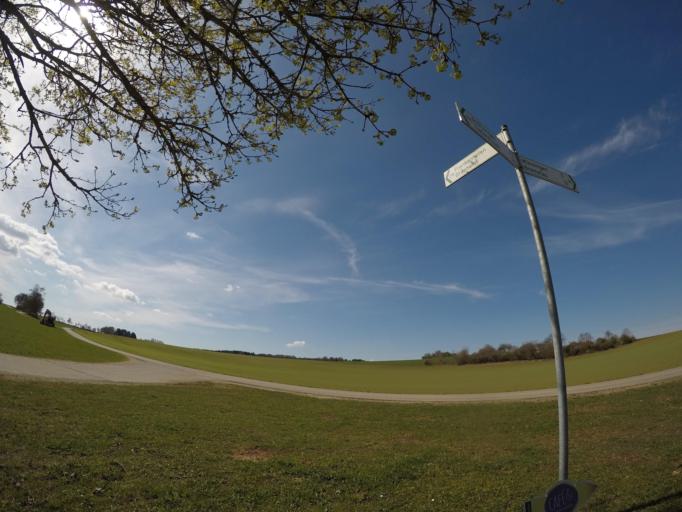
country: DE
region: Baden-Wuerttemberg
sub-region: Tuebingen Region
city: Mehrstetten
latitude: 48.3450
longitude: 9.5740
